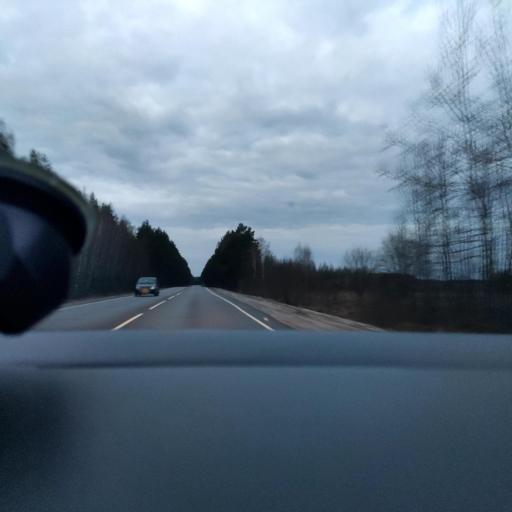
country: RU
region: Moskovskaya
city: Krasnyy Tkach
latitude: 55.4191
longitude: 39.1815
